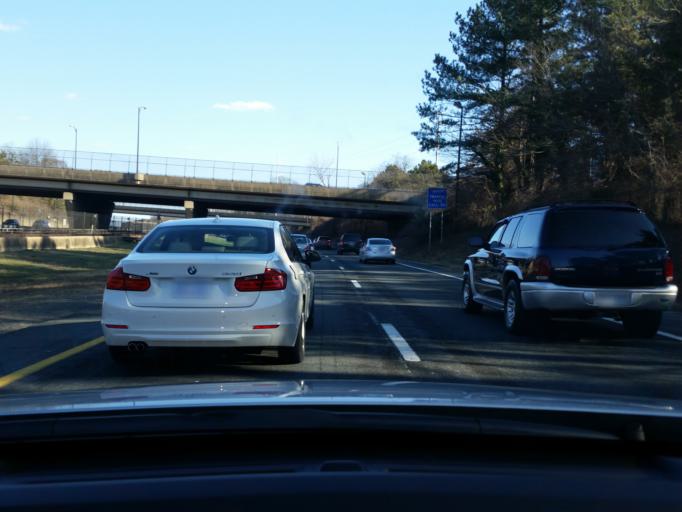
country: US
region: Virginia
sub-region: City of Falls Church
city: Falls Church
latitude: 38.8884
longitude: -77.1627
